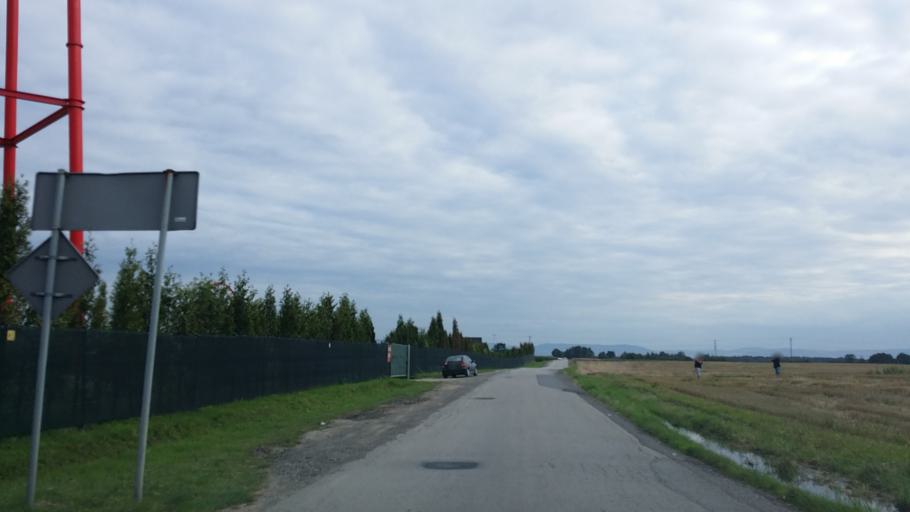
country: PL
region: Lesser Poland Voivodeship
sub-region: Powiat oswiecimski
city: Przeciszow
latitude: 50.0022
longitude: 19.4045
